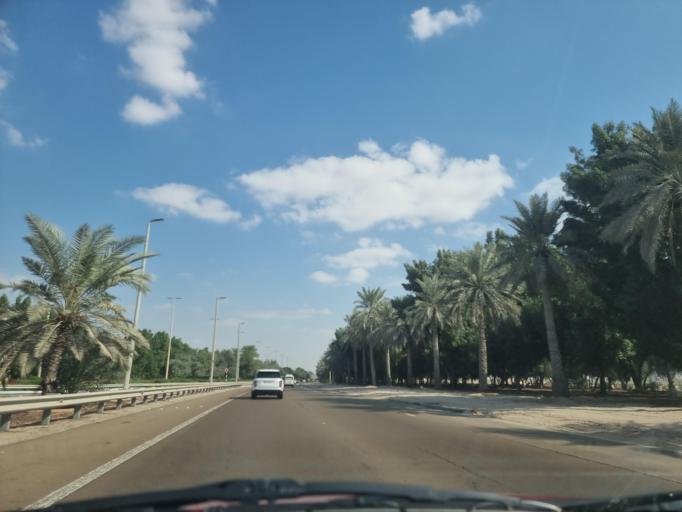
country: AE
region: Abu Dhabi
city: Abu Dhabi
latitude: 24.4103
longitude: 54.6392
